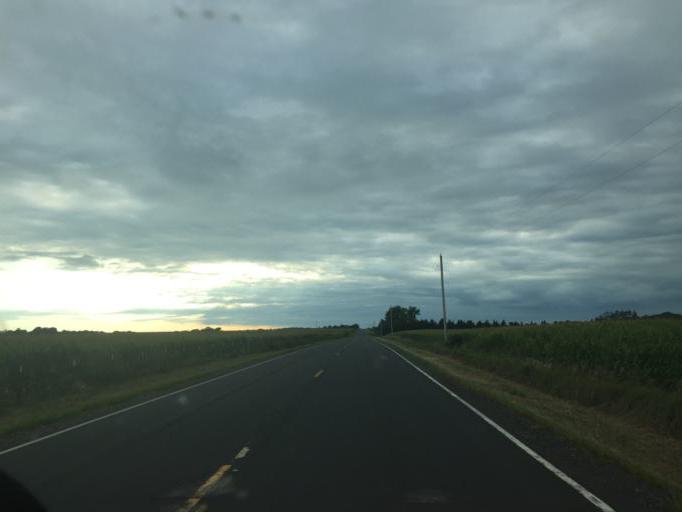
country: US
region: Minnesota
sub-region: Olmsted County
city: Rochester
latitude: 43.9640
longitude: -92.5028
